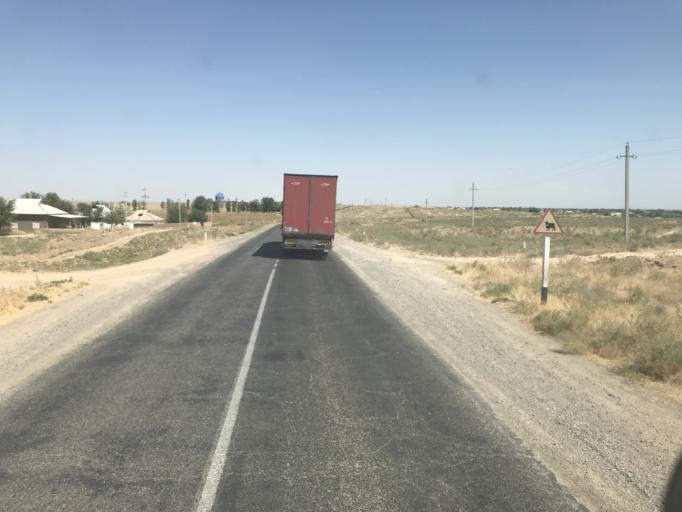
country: UZ
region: Toshkent
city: Chinoz
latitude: 41.3267
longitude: 68.6791
